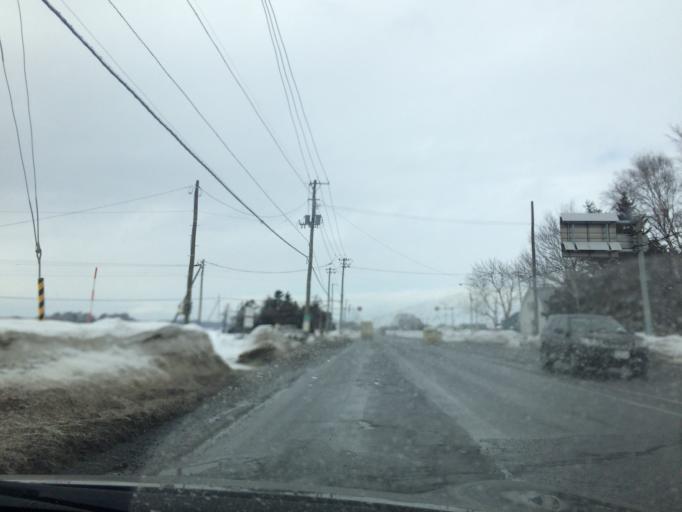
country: JP
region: Hokkaido
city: Kitahiroshima
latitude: 43.0114
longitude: 141.5631
